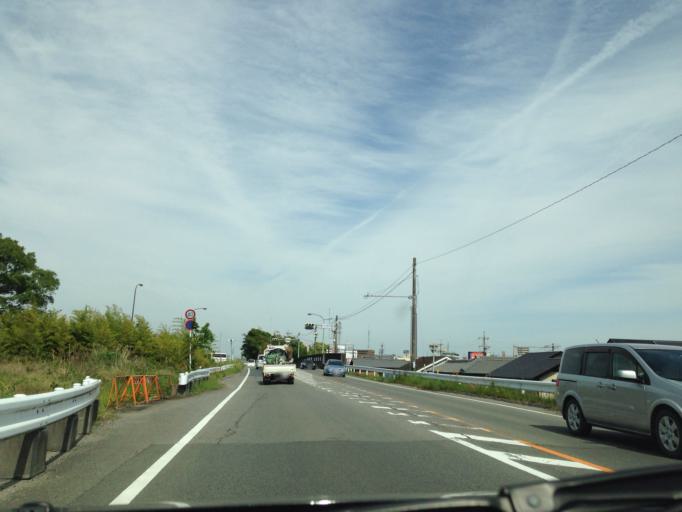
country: JP
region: Mie
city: Yokkaichi
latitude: 34.9759
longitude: 136.6016
